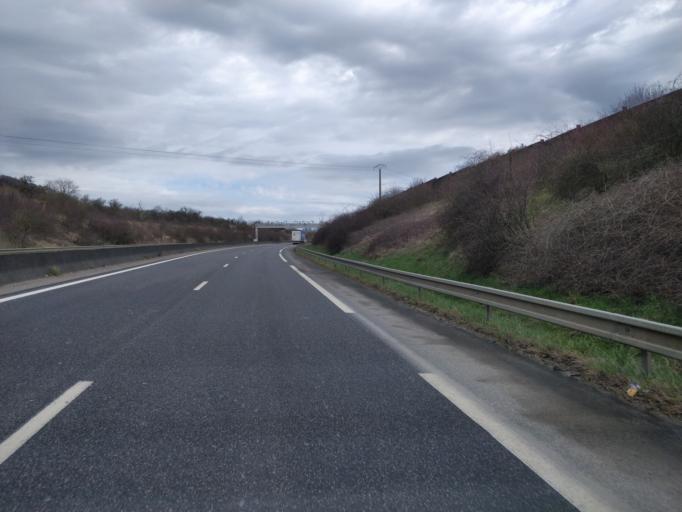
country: FR
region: Lorraine
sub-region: Departement de la Moselle
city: Vitry-sur-Orne
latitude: 49.2712
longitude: 6.1115
